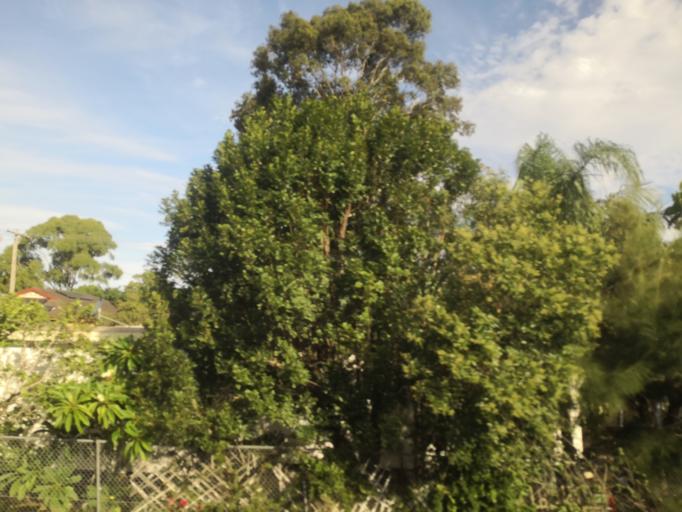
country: AU
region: New South Wales
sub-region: Gosford Shire
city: Blackwall
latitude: -33.4932
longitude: 151.3141
